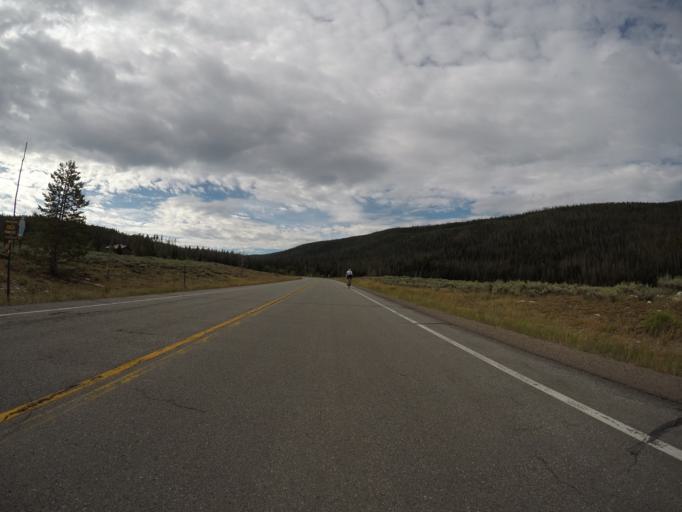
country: US
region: Wyoming
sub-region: Carbon County
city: Saratoga
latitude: 41.3429
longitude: -106.5265
